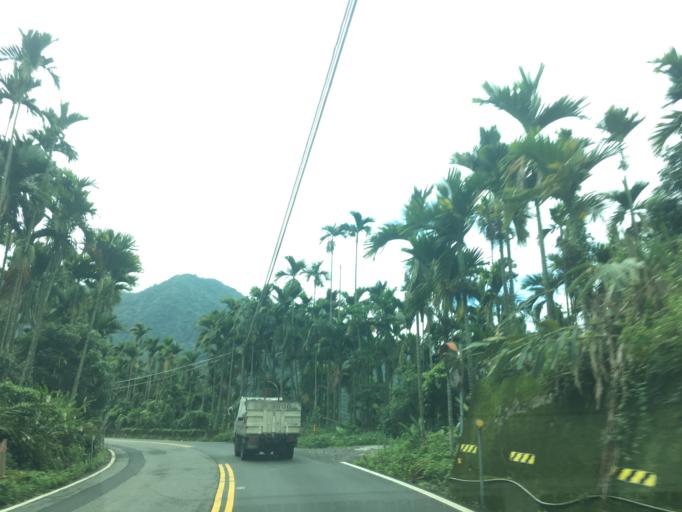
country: TW
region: Taiwan
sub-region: Chiayi
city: Jiayi Shi
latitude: 23.5595
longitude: 120.5773
